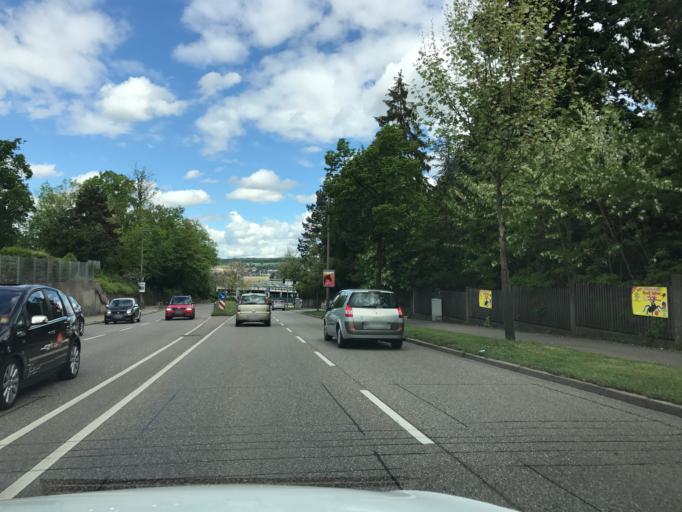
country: DE
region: Baden-Wuerttemberg
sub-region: Regierungsbezirk Stuttgart
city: Bietigheim-Bissingen
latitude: 48.9457
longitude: 9.1390
